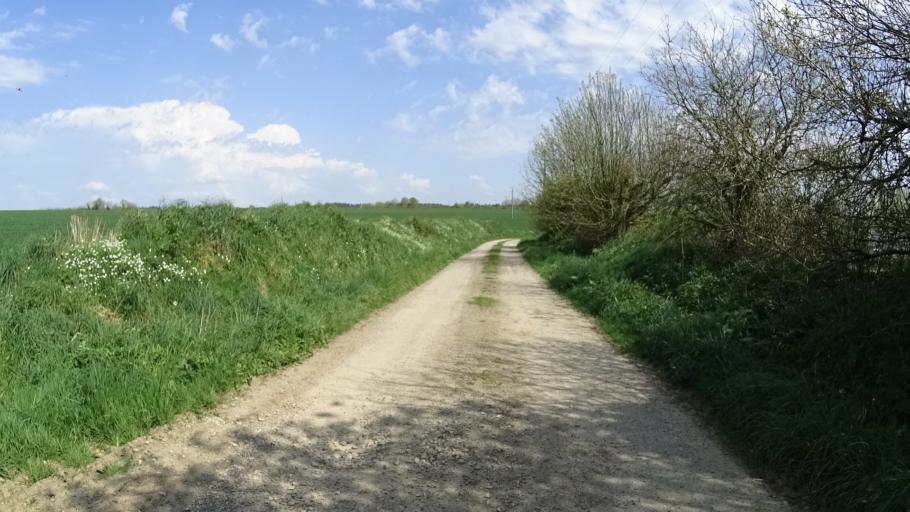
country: FR
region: Brittany
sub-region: Departement du Finistere
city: Sizun
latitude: 48.4192
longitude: -4.0915
